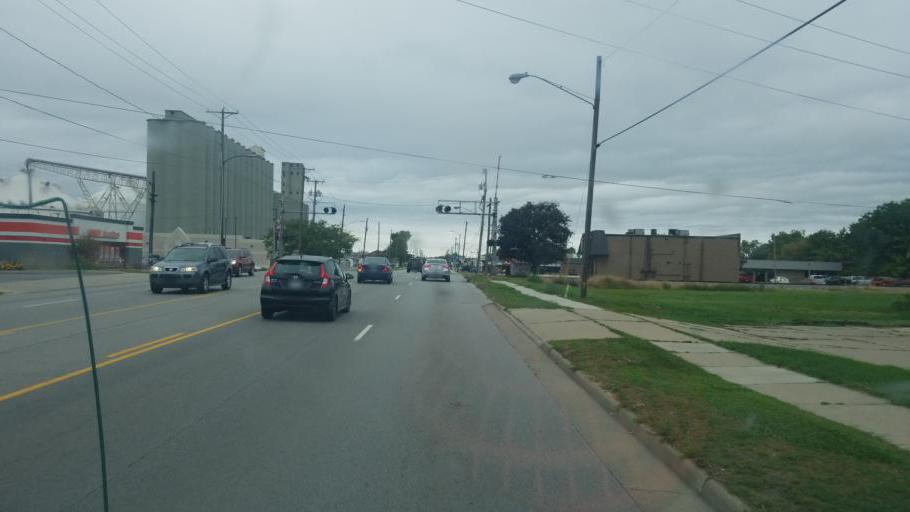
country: US
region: Ohio
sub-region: Lucas County
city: Maumee
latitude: 41.5691
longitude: -83.6572
